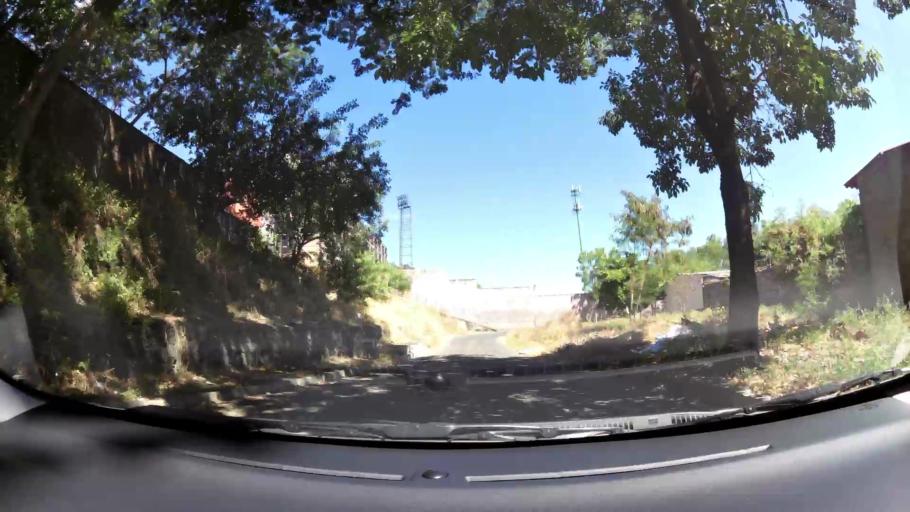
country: SV
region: San Miguel
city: San Miguel
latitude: 13.4822
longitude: -88.1687
